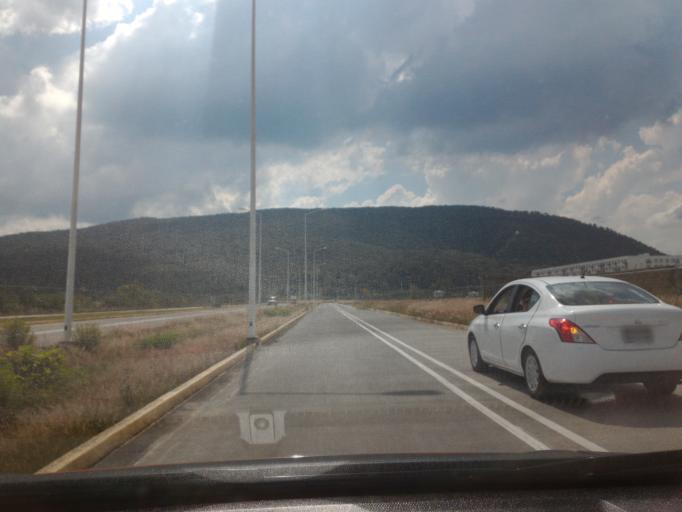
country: MX
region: Jalisco
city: Nuevo Mexico
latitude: 20.6898
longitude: -103.4689
